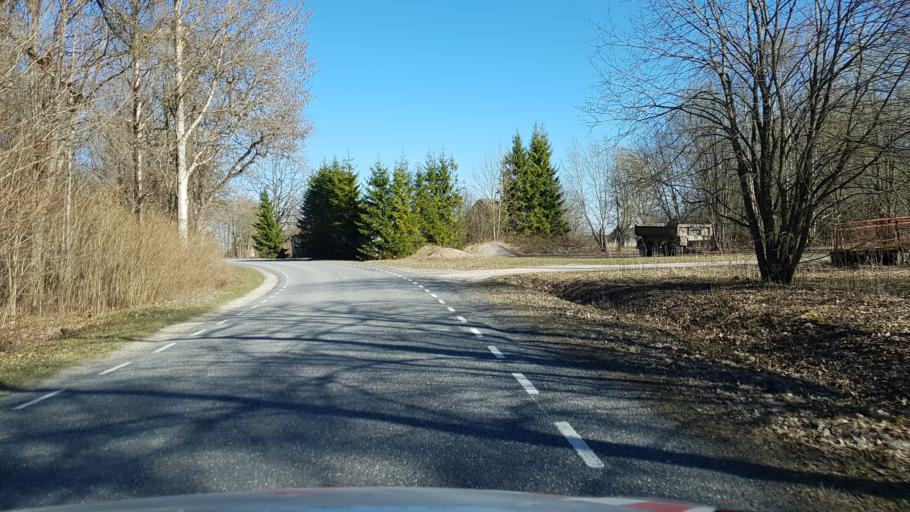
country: EE
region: Jaervamaa
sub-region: Koeru vald
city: Koeru
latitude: 59.0078
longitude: 26.1101
